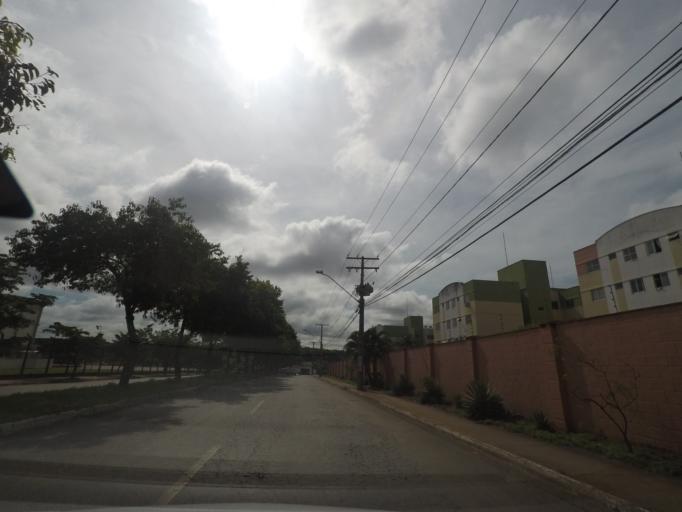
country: BR
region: Goias
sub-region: Goiania
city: Goiania
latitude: -16.6597
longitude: -49.2119
